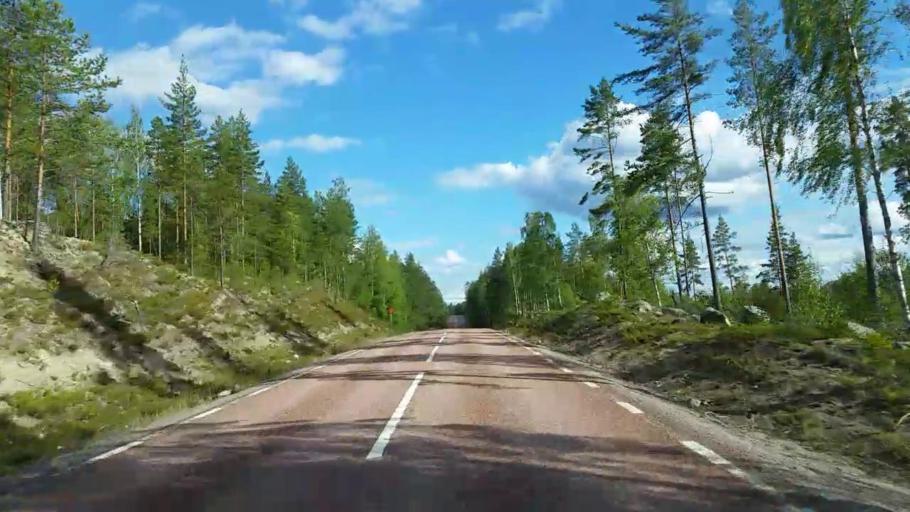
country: SE
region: Gaevleborg
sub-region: Ljusdals Kommun
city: Farila
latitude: 62.0973
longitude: 15.7922
